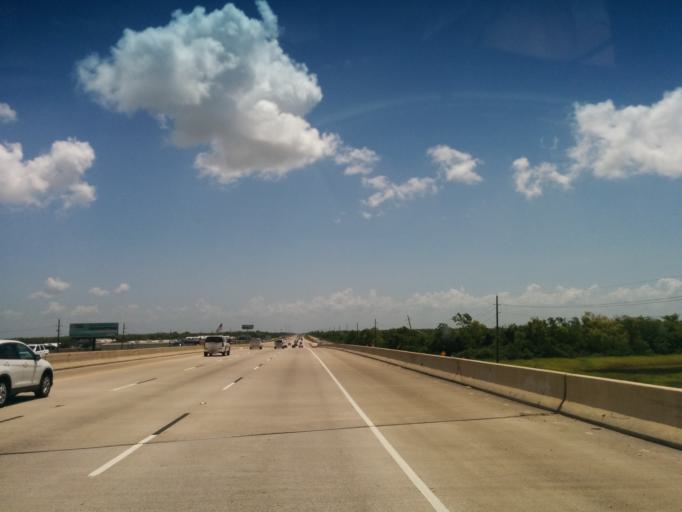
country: US
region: Texas
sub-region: Chambers County
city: Mont Belvieu
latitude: 29.8243
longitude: -94.8661
